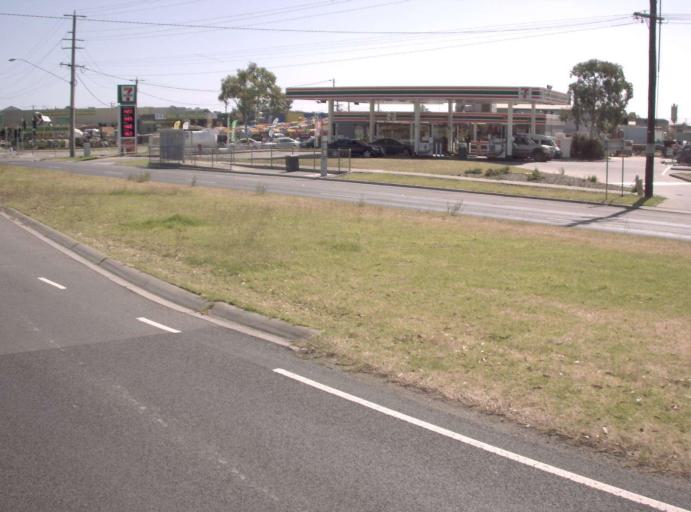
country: AU
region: Victoria
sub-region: Frankston
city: Carrum Downs
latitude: -38.1047
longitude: 145.1685
